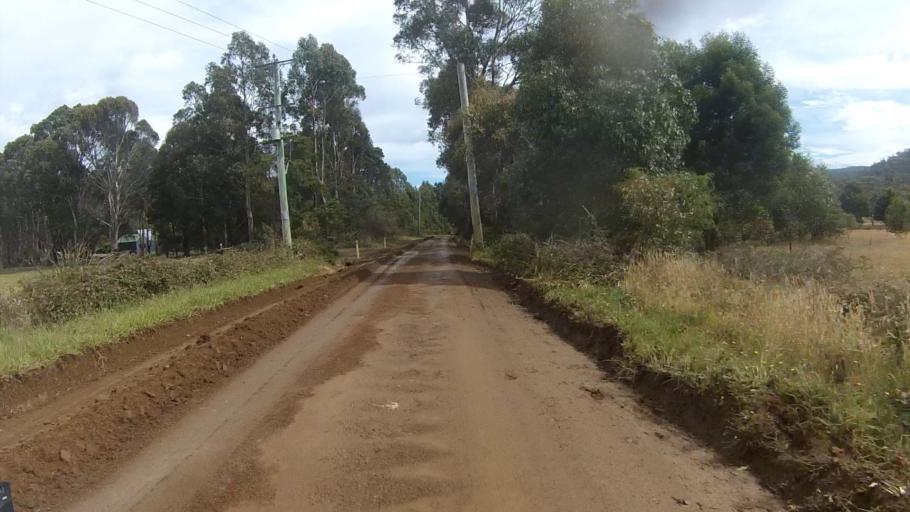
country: AU
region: Tasmania
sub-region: Sorell
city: Sorell
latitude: -42.7733
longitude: 147.8089
